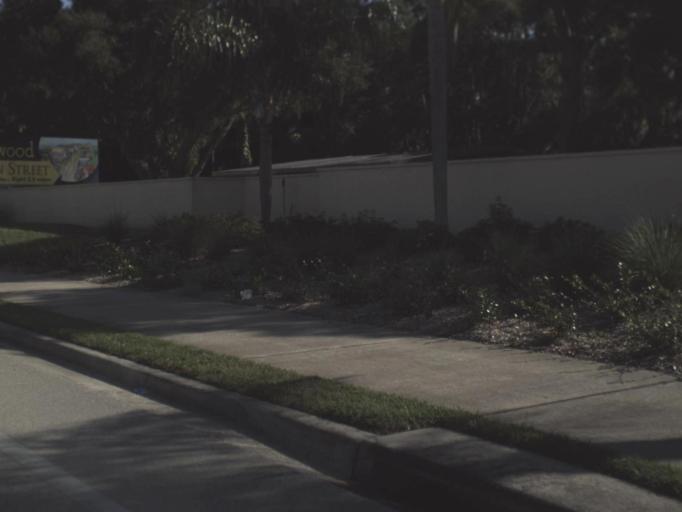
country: US
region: Florida
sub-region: Sarasota County
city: Englewood
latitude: 26.9927
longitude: -82.3701
